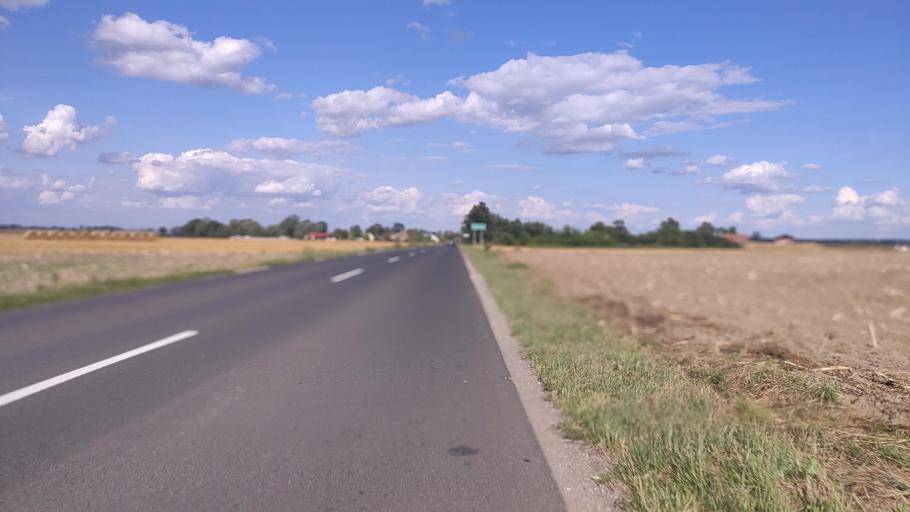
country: PL
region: Greater Poland Voivodeship
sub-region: Powiat poznanski
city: Swarzedz
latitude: 52.4217
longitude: 17.1481
